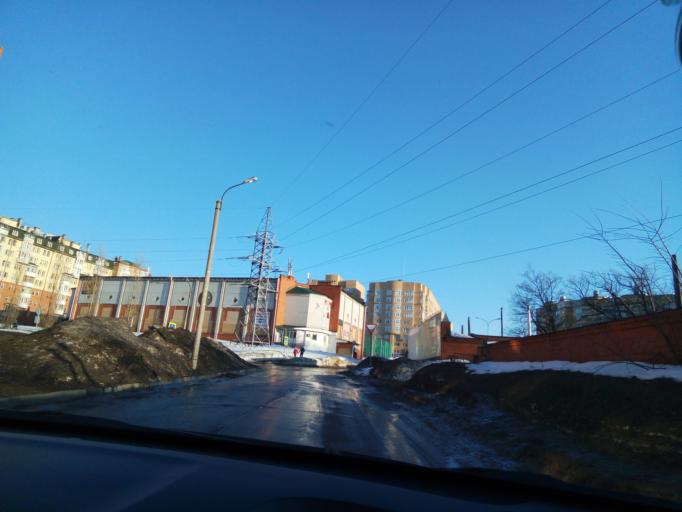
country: RU
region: Chuvashia
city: Novyye Lapsary
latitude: 56.1352
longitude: 47.1578
